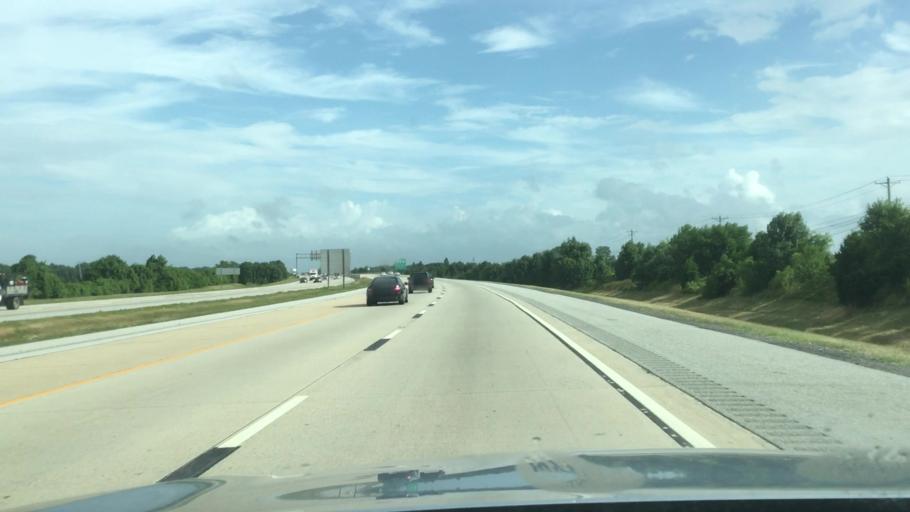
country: US
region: Delaware
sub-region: New Castle County
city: Delaware City
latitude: 39.5164
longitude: -75.6517
